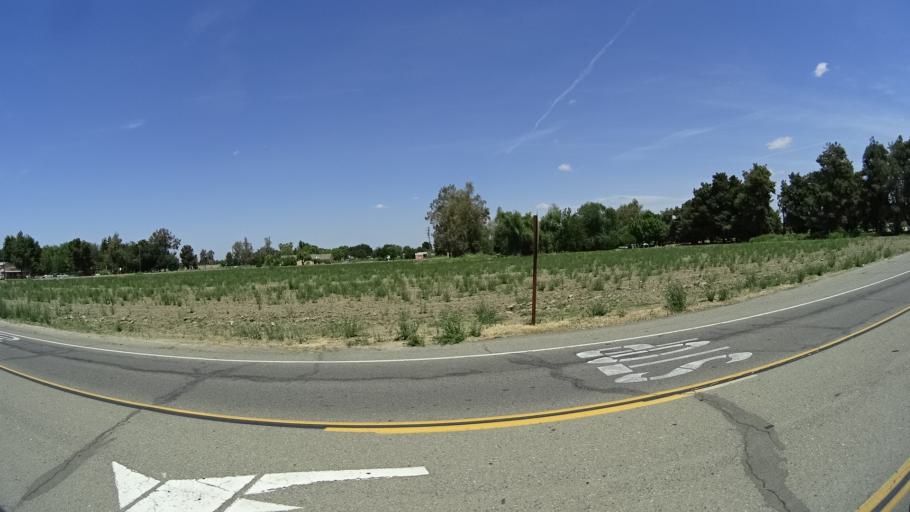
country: US
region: California
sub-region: Kings County
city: Lemoore
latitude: 36.2982
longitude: -119.7614
